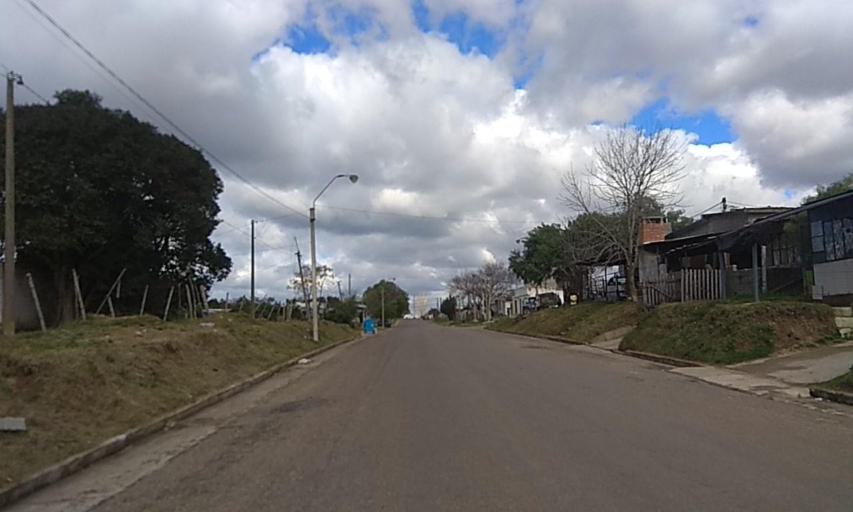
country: UY
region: Florida
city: Florida
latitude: -34.0884
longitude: -56.2279
